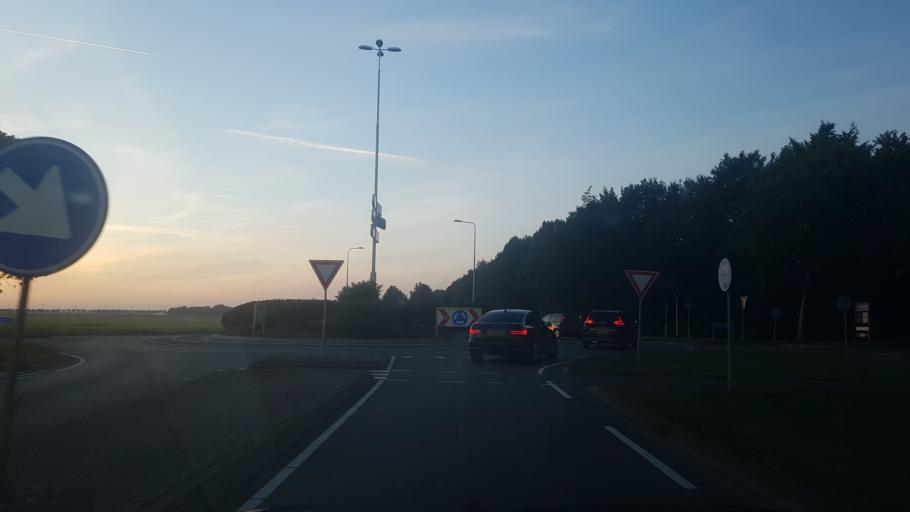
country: NL
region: Flevoland
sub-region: Gemeente Noordoostpolder
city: Emmeloord
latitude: 52.7084
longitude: 5.7196
